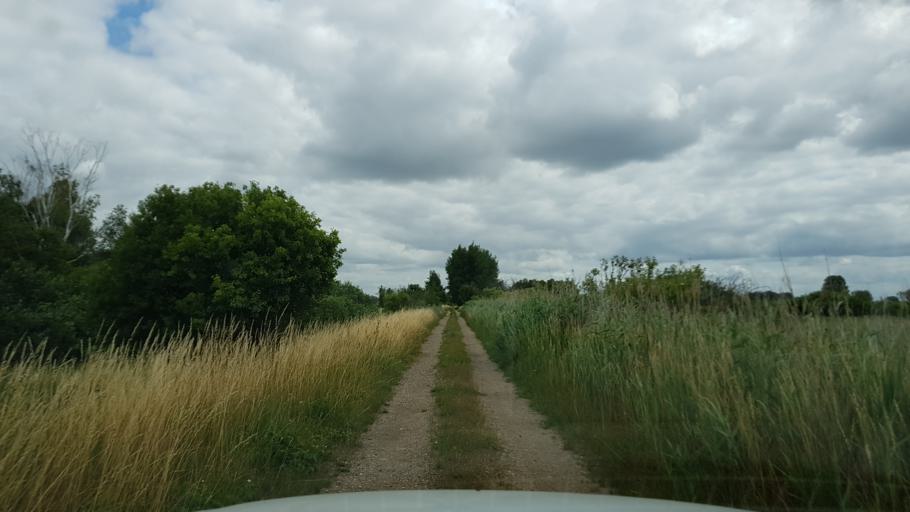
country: PL
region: West Pomeranian Voivodeship
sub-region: Powiat mysliborski
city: Mysliborz
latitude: 52.9441
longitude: 14.9320
